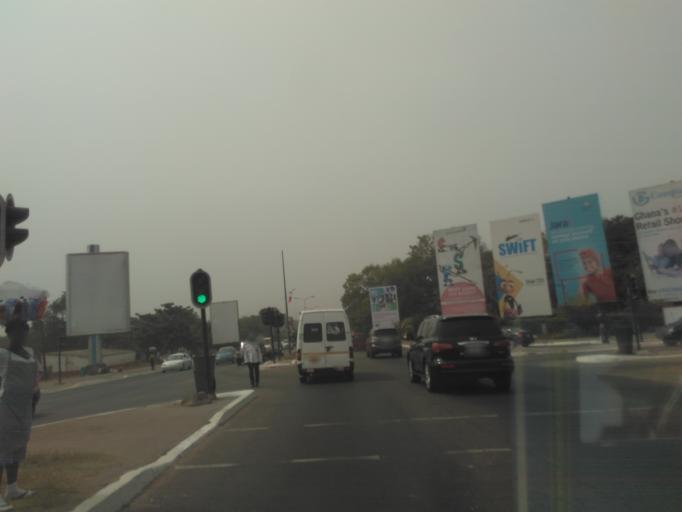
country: GH
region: Greater Accra
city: Accra
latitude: 5.5760
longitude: -0.1882
